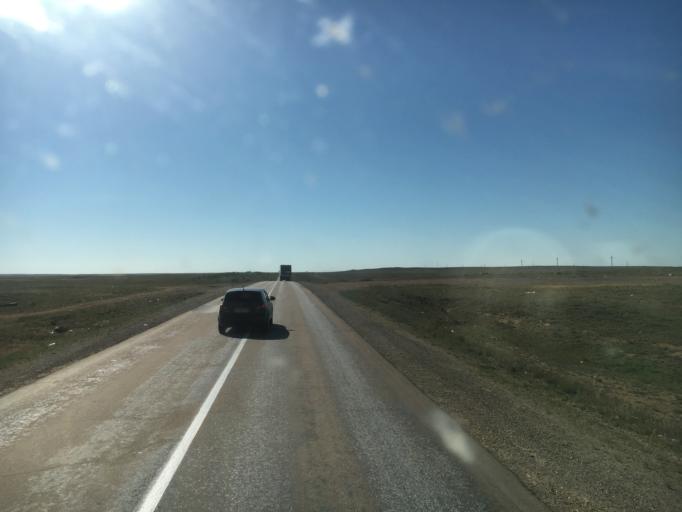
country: RU
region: Orenburg
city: Dombarovskiy
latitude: 50.0816
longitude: 59.5699
